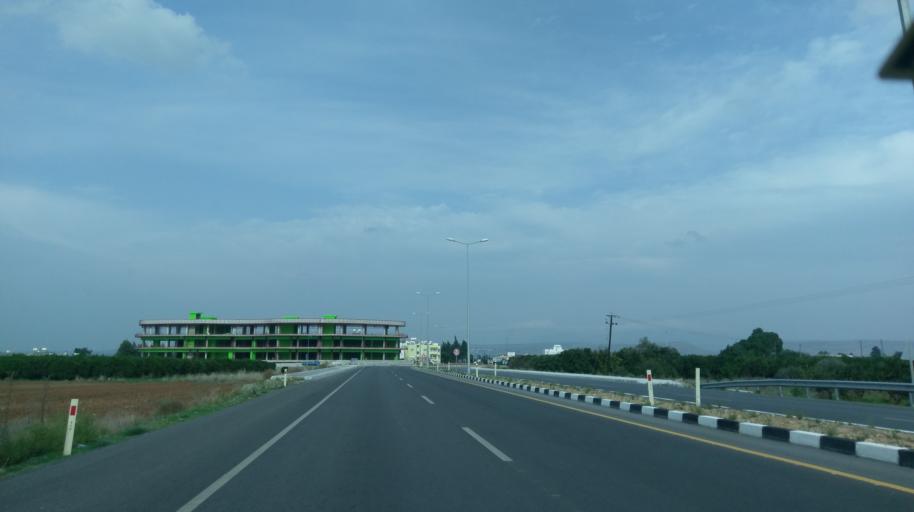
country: CY
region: Lefkosia
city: Morfou
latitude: 35.1890
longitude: 33.0020
